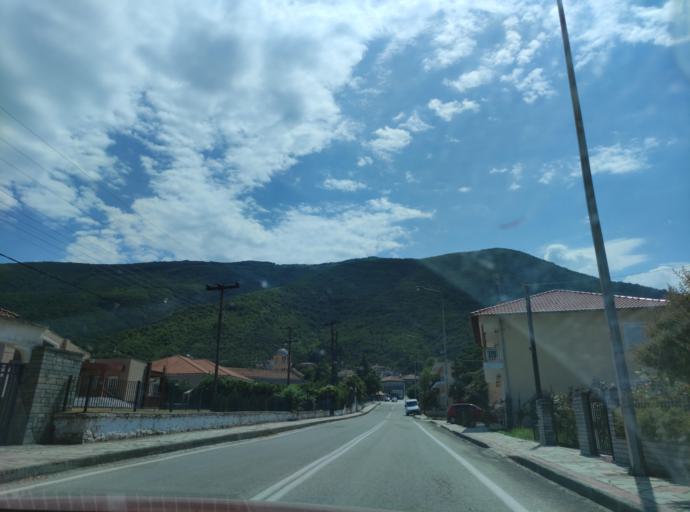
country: GR
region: East Macedonia and Thrace
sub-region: Nomos Kavalas
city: Palaiochori
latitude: 40.9477
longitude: 24.2116
